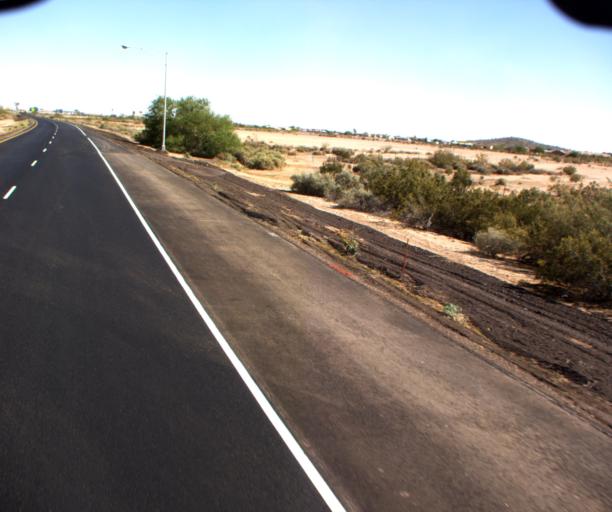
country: US
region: Arizona
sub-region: Pinal County
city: Arizona City
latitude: 32.8202
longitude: -111.6891
